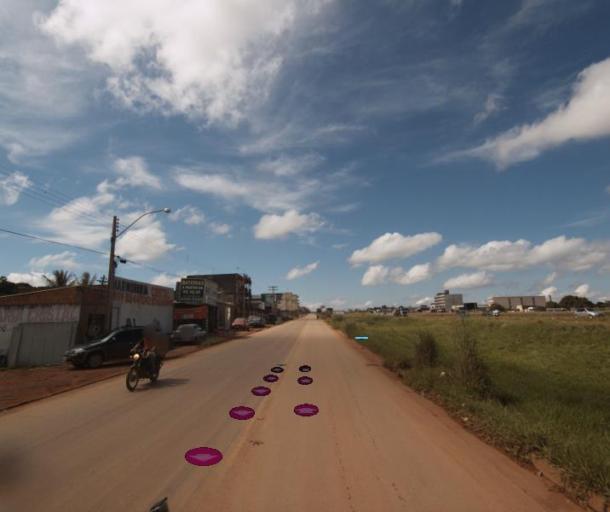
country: BR
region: Federal District
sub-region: Brasilia
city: Brasilia
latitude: -15.7413
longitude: -48.2696
